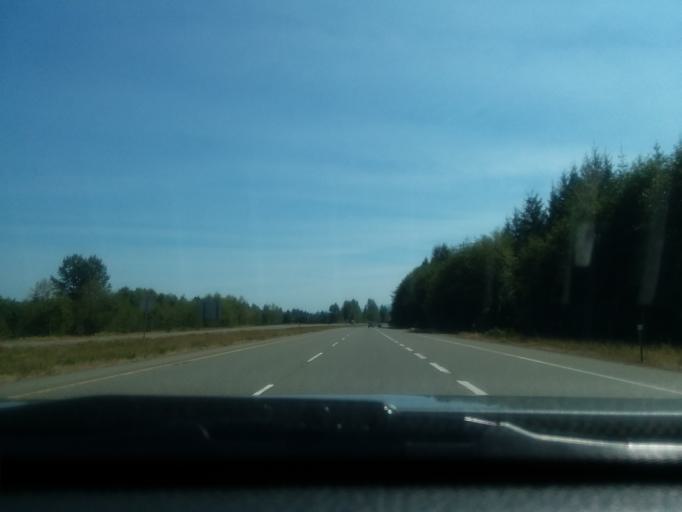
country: CA
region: British Columbia
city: Cumberland
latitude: 49.5207
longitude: -124.8557
